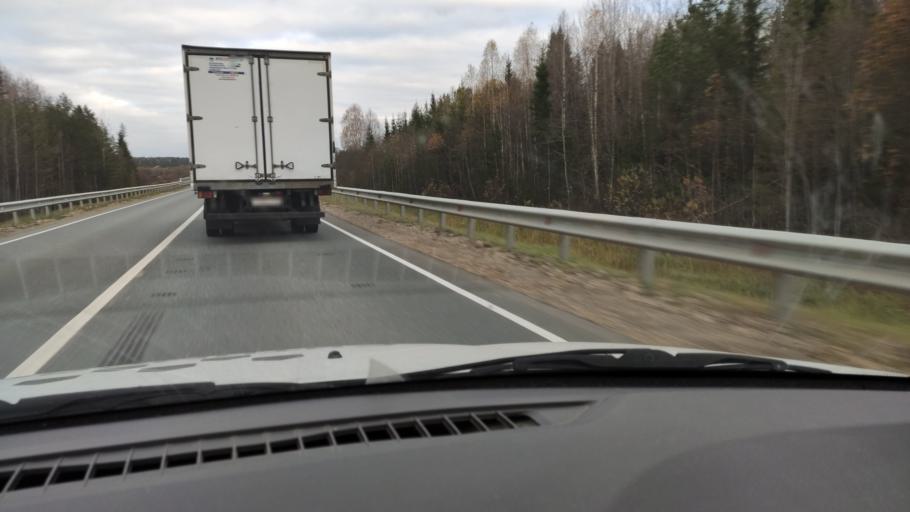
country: RU
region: Kirov
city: Chernaya Kholunitsa
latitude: 58.8590
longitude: 51.6870
